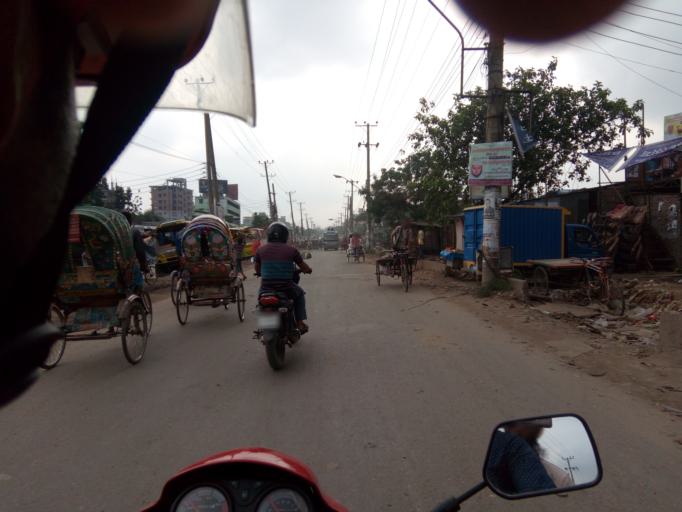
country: BD
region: Dhaka
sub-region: Dhaka
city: Dhaka
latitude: 23.7123
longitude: 90.4498
